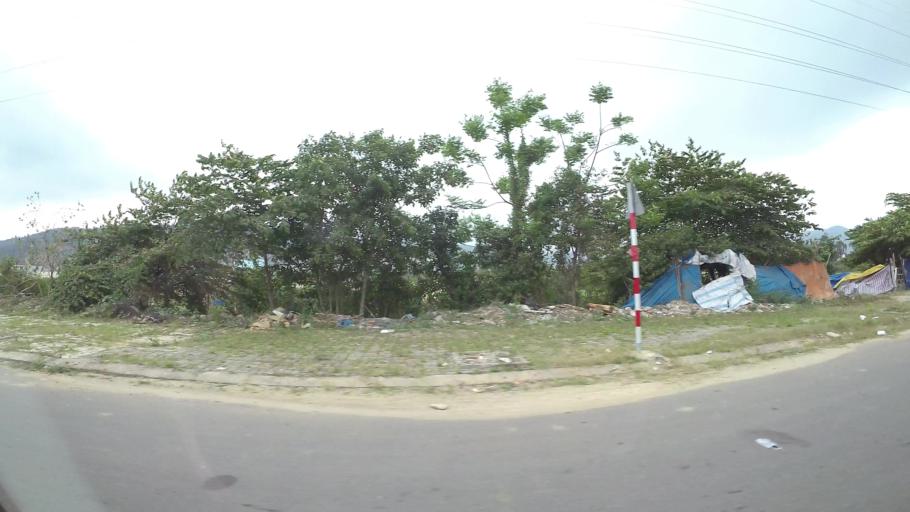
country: VN
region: Da Nang
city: Lien Chieu
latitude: 16.0504
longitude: 108.1668
